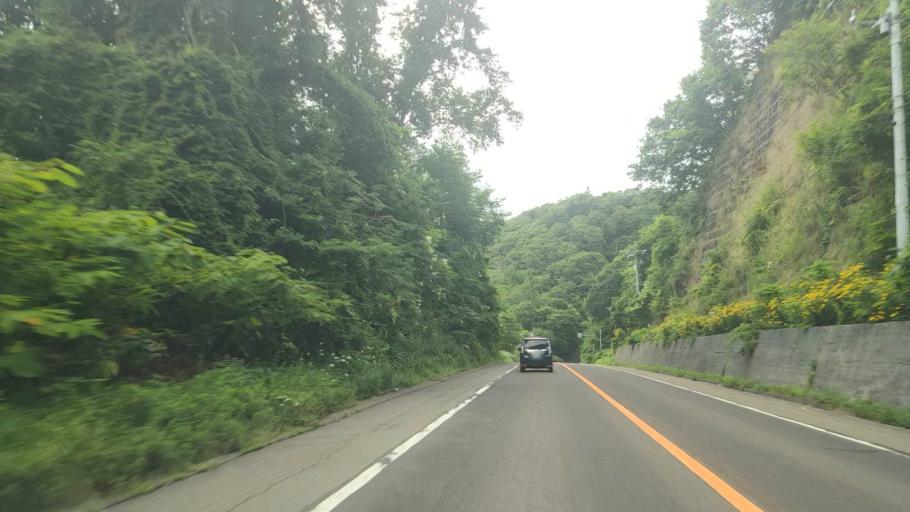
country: JP
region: Hokkaido
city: Niseko Town
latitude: 42.5899
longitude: 140.6765
